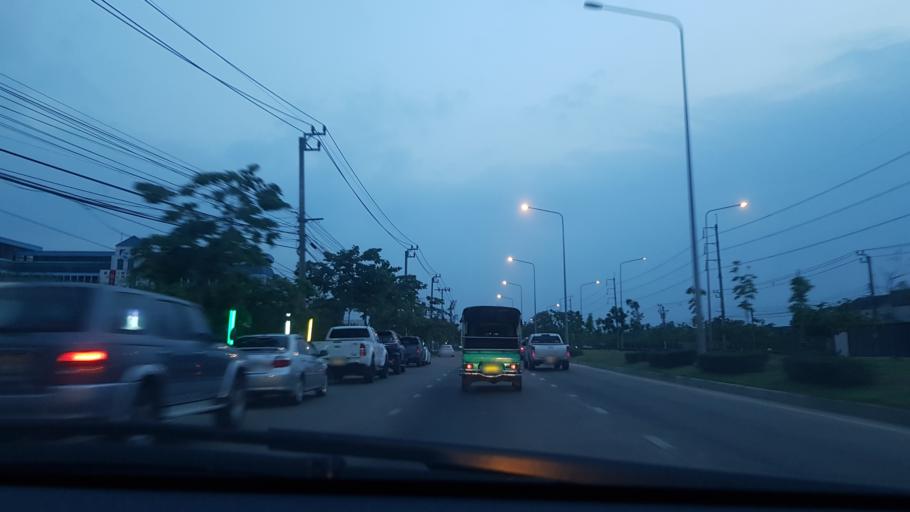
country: TH
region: Bangkok
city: Nong Khaem
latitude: 13.7447
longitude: 100.3639
